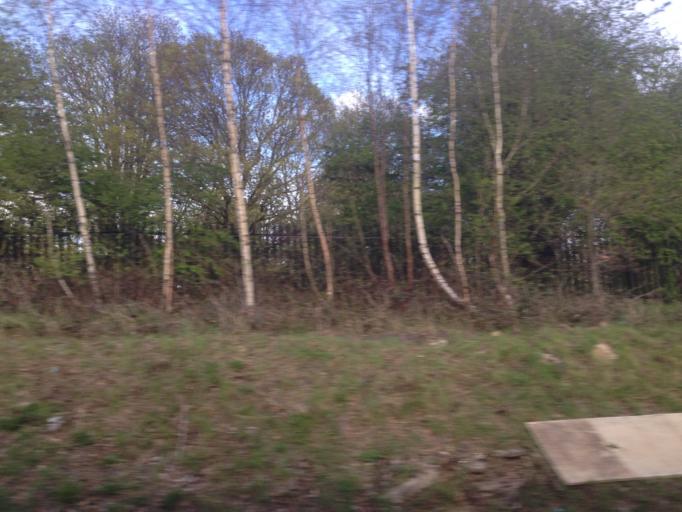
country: GB
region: England
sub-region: Greater London
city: Brixton Hill
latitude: 51.4332
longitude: -0.1389
